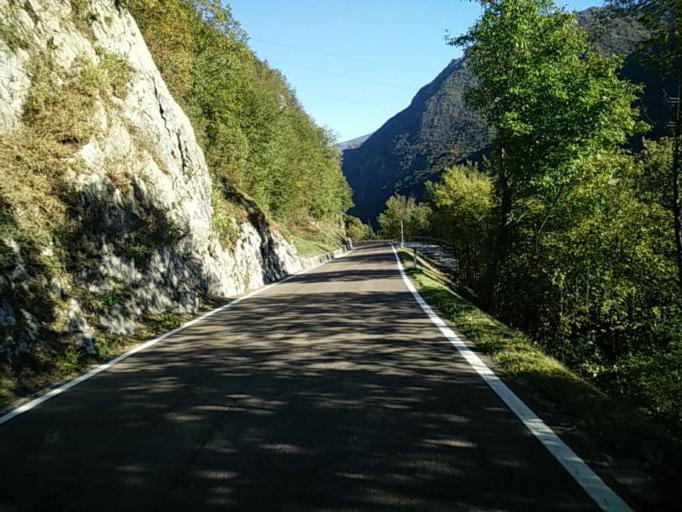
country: IT
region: Trentino-Alto Adige
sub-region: Provincia di Trento
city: Molina di Ledro
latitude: 45.8697
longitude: 10.7846
